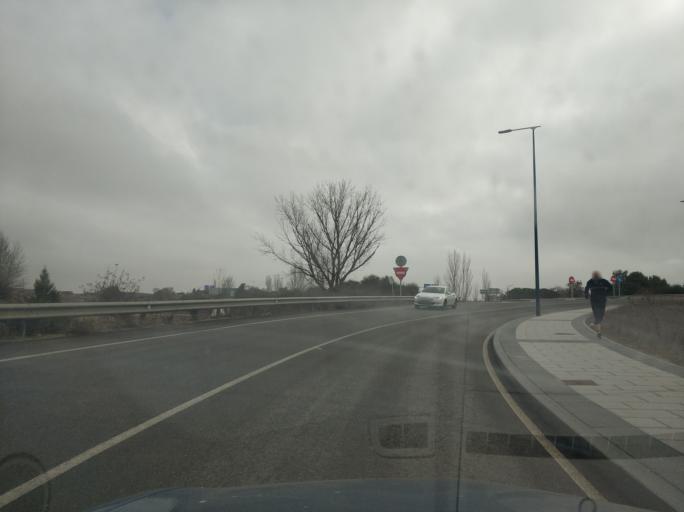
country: ES
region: Castille and Leon
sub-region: Provincia de Valladolid
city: Arroyo
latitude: 41.6138
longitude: -4.7969
